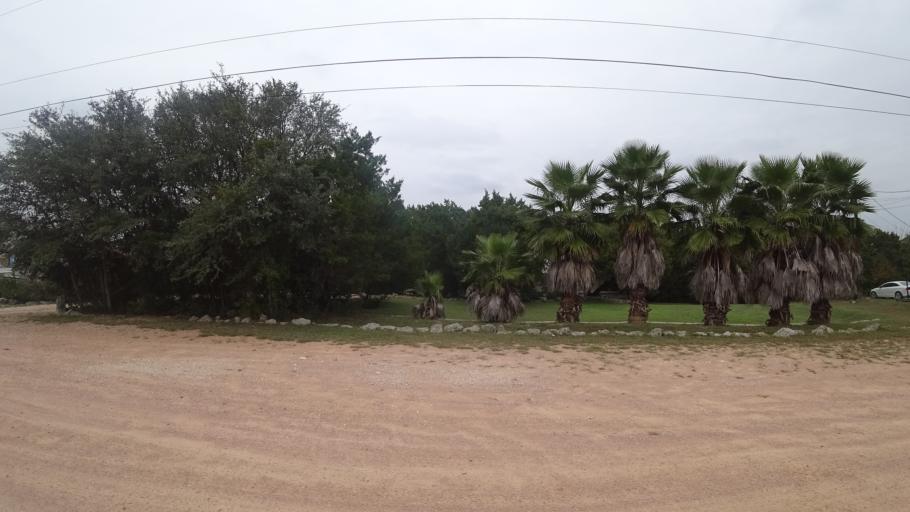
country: US
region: Texas
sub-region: Travis County
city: Hudson Bend
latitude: 30.3789
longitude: -97.9376
